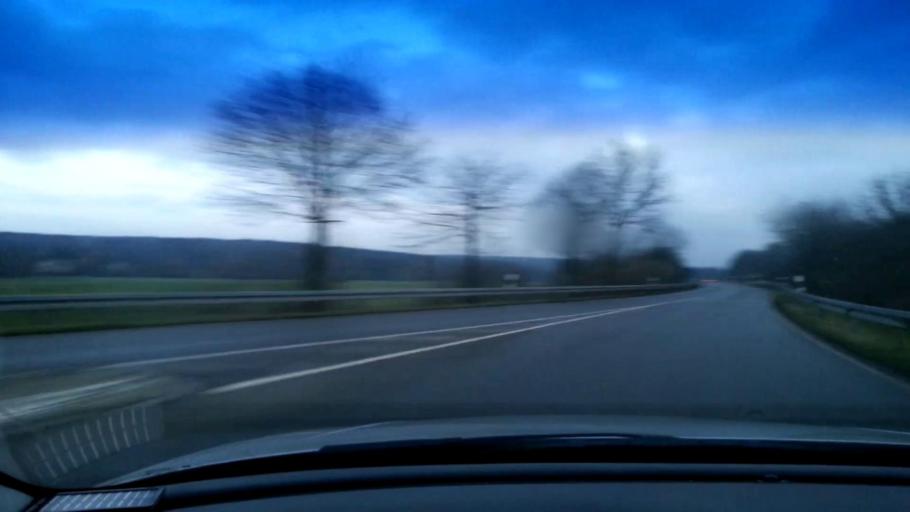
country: DE
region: Bavaria
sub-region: Upper Franconia
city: Frensdorf
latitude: 49.8499
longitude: 10.8789
